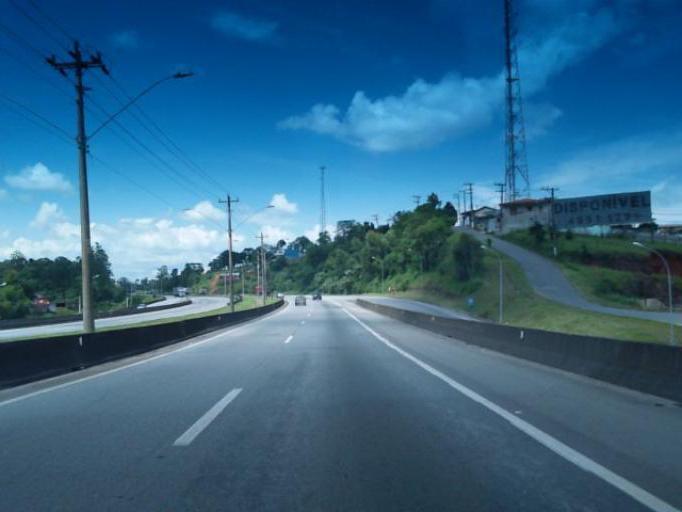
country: BR
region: Sao Paulo
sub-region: Sao Lourenco Da Serra
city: Sao Lourenco da Serra
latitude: -23.8589
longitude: -46.9448
